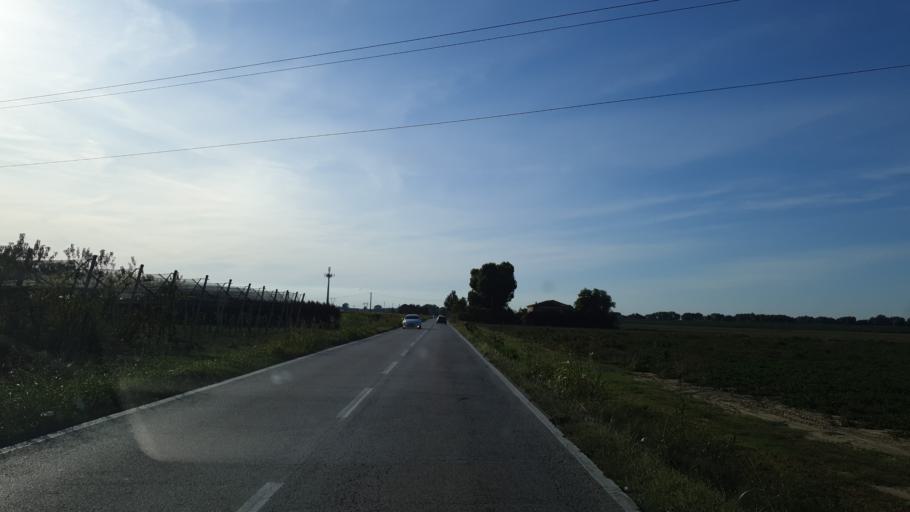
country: IT
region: Emilia-Romagna
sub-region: Provincia di Ravenna
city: Voltana
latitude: 44.5499
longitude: 11.9559
